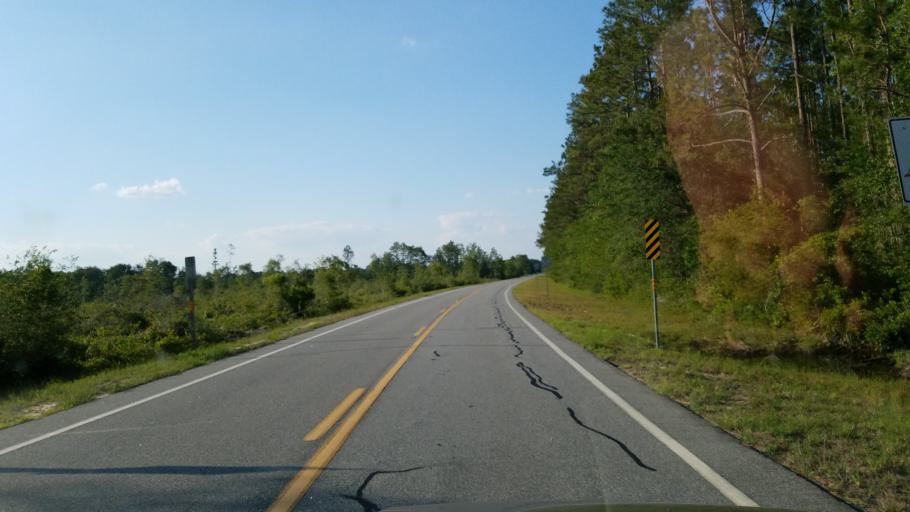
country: US
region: Georgia
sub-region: Echols County
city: Statenville
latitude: 30.8484
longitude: -83.0529
